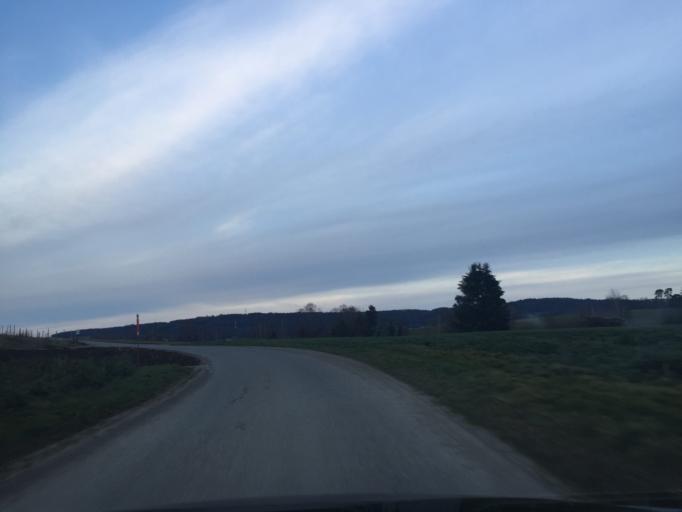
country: CH
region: Thurgau
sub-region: Frauenfeld District
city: Diessenhofen
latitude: 47.6741
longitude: 8.7421
